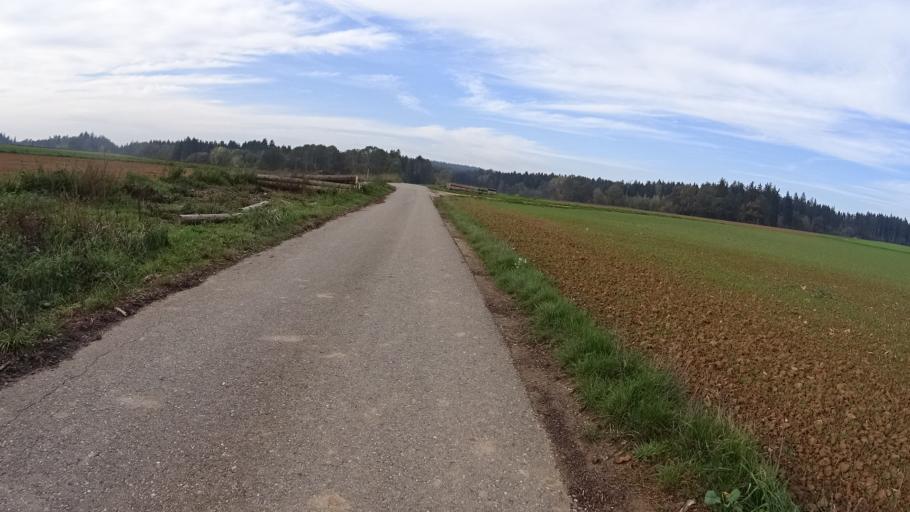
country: DE
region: Bavaria
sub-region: Upper Bavaria
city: Buxheim
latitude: 48.8305
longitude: 11.2717
